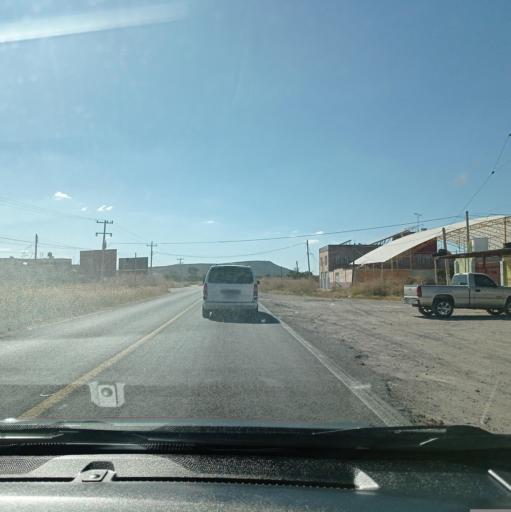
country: MX
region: Jalisco
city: San Miguel el Alto
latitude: 21.0270
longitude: -102.4172
